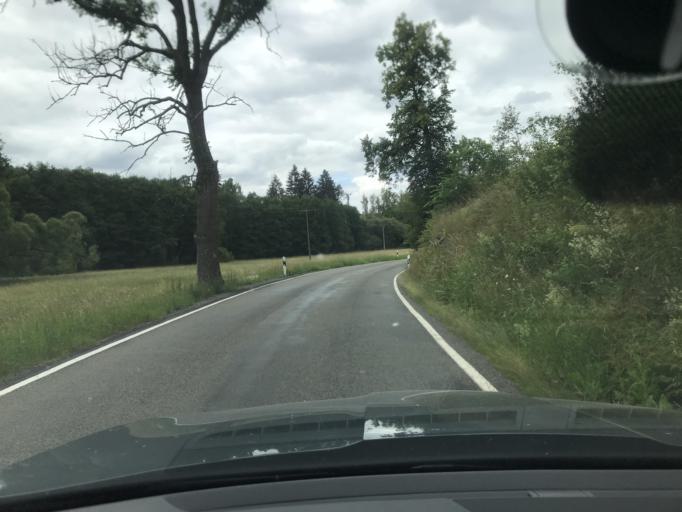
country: DE
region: Saxony-Anhalt
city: Friedrichsbrunn
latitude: 51.6243
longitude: 11.0701
